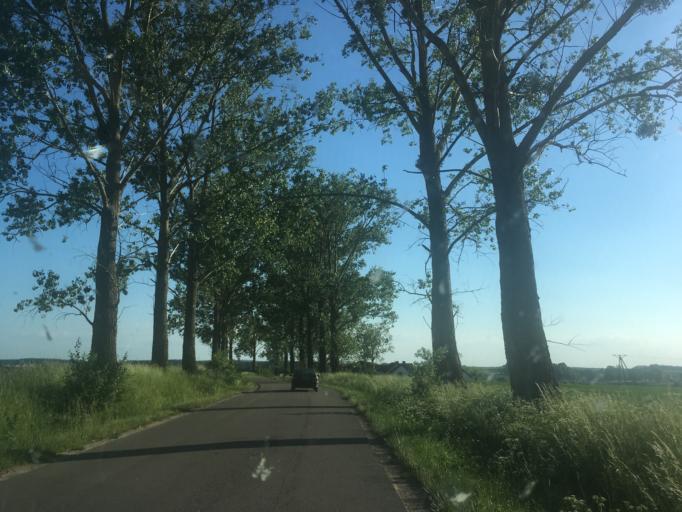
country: PL
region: Warmian-Masurian Voivodeship
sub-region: Powiat ostrodzki
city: Ostroda
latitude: 53.6752
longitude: 20.0401
